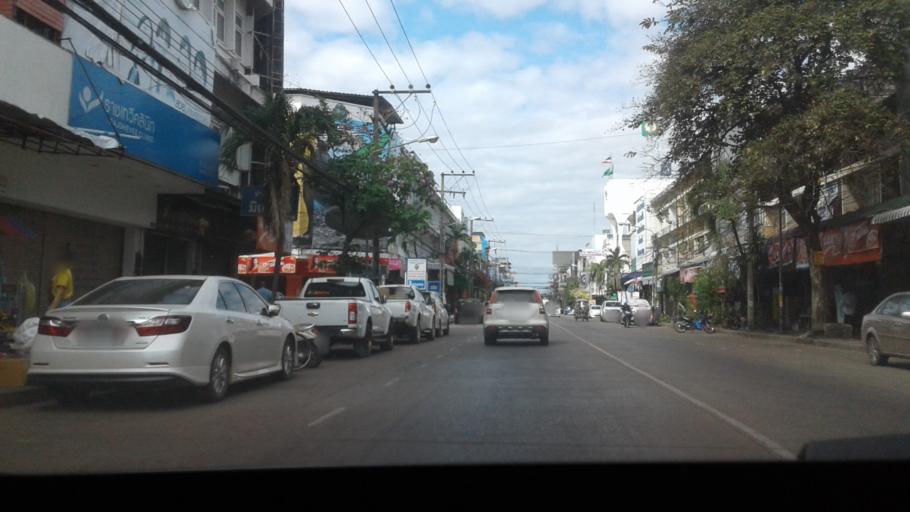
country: TH
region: Changwat Udon Thani
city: Udon Thani
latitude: 17.4066
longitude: 102.7896
